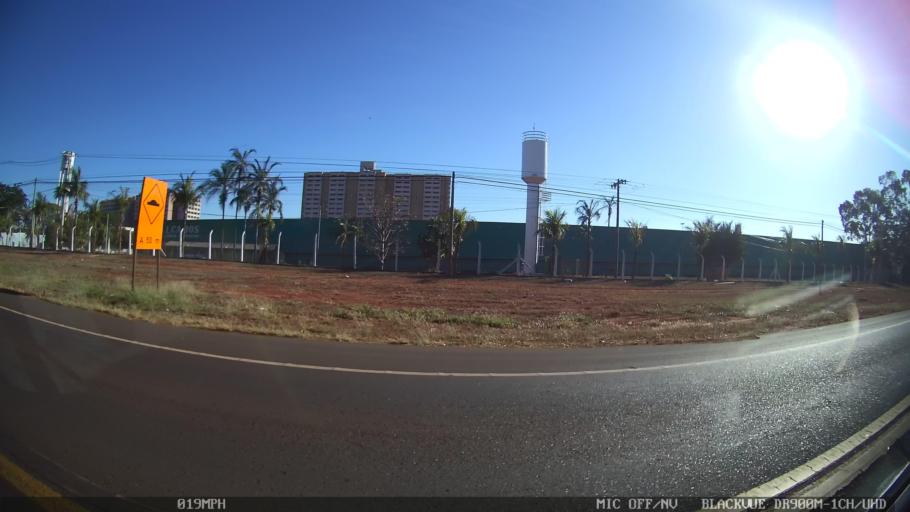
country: BR
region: Sao Paulo
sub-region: Olimpia
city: Olimpia
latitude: -20.7137
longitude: -48.9087
